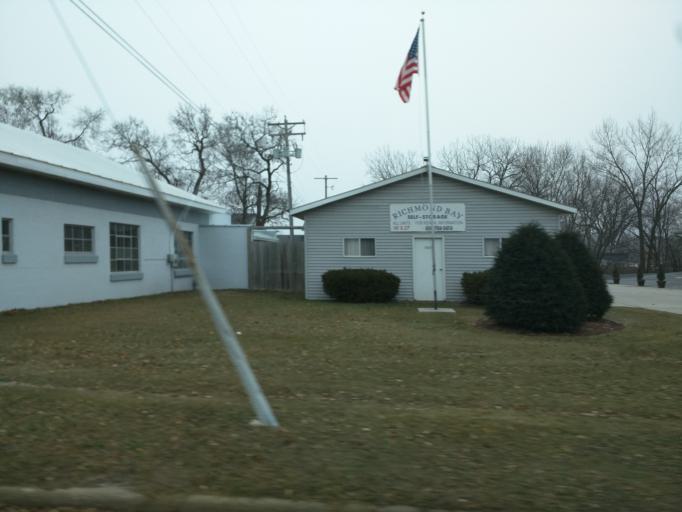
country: US
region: Wisconsin
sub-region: La Crosse County
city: North La Crosse
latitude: 43.8428
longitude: -91.2615
